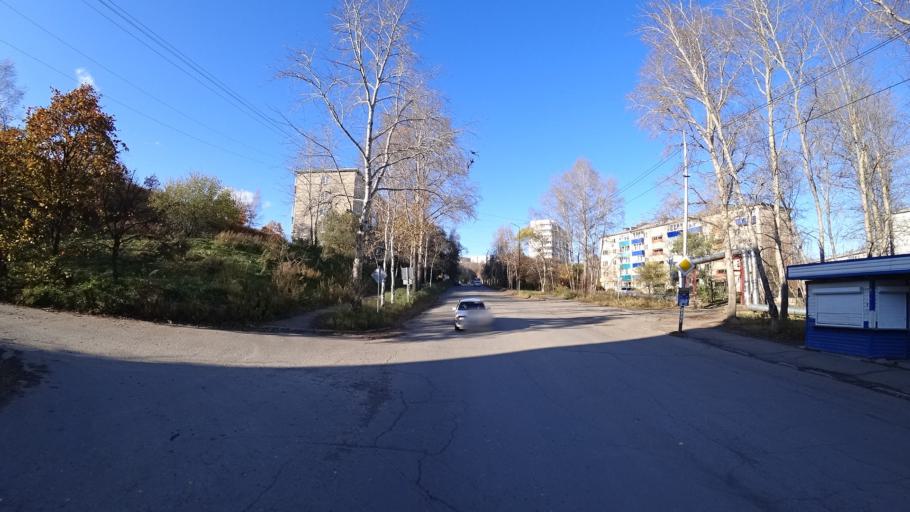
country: RU
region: Khabarovsk Krai
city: Amursk
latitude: 50.2362
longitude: 136.9053
